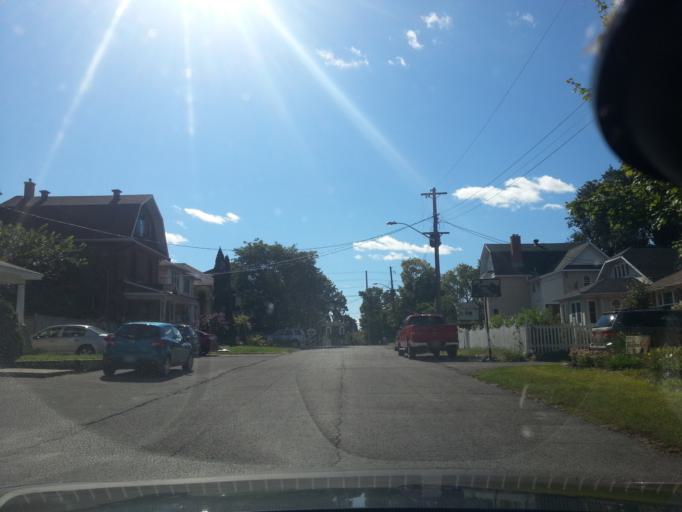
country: CA
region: Ontario
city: Ottawa
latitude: 45.3860
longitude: -75.7486
